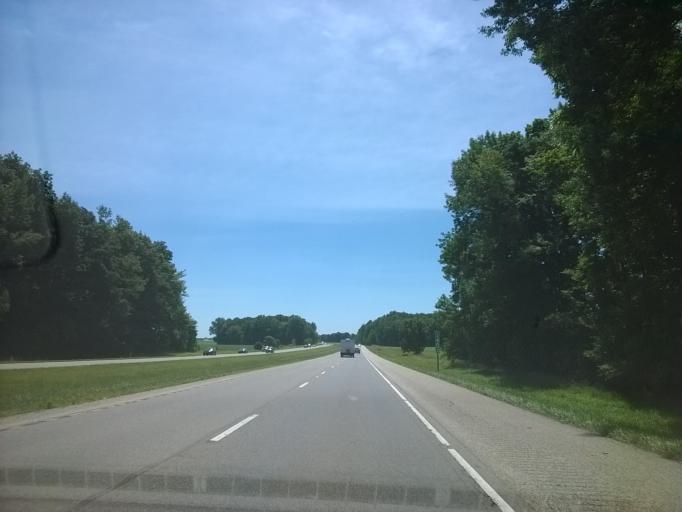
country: US
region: Indiana
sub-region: Decatur County
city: Greensburg
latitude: 39.3251
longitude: -85.3807
